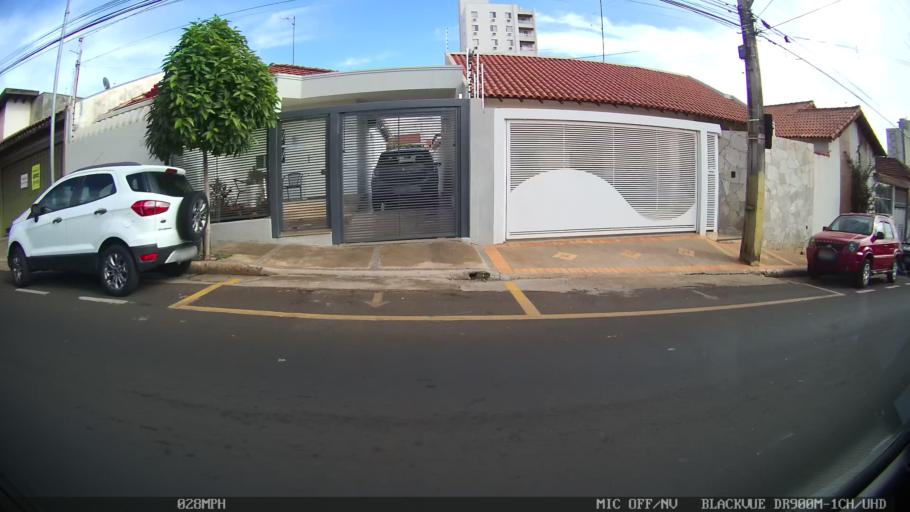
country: BR
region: Sao Paulo
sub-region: Catanduva
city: Catanduva
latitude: -21.1341
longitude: -48.9789
